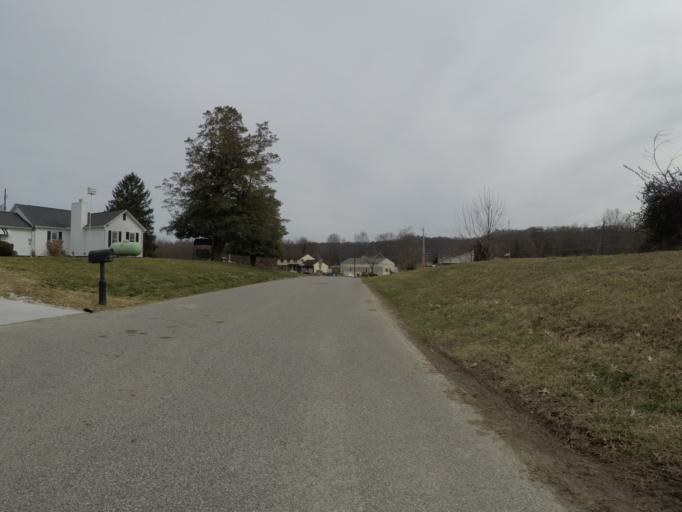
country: US
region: West Virginia
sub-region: Cabell County
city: Pea Ridge
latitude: 38.4501
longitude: -82.3305
